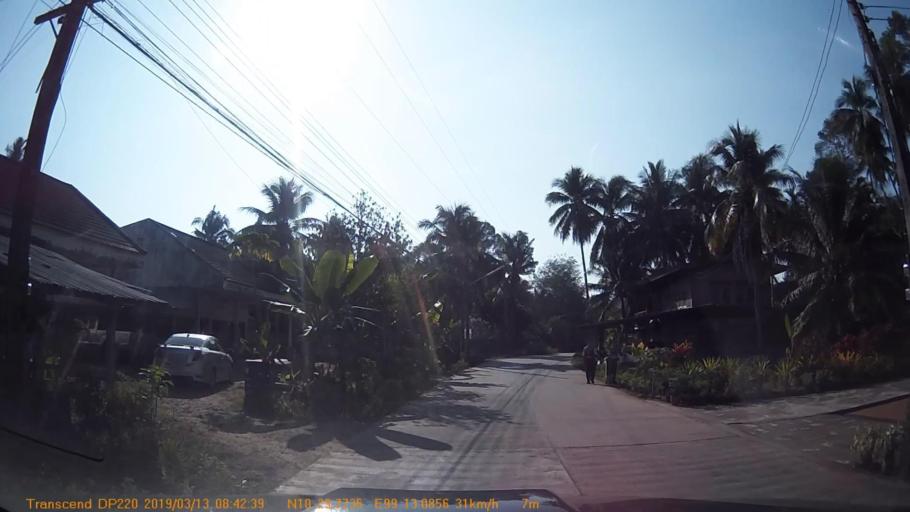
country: TH
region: Chumphon
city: Chumphon
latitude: 10.4961
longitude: 99.2182
